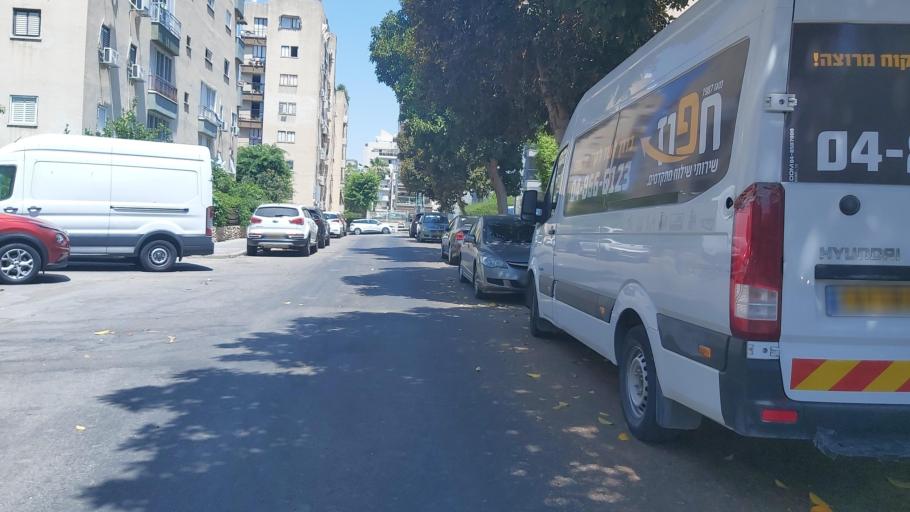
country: IL
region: Central District
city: Rishon LeZiyyon
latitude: 31.9626
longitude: 34.8087
